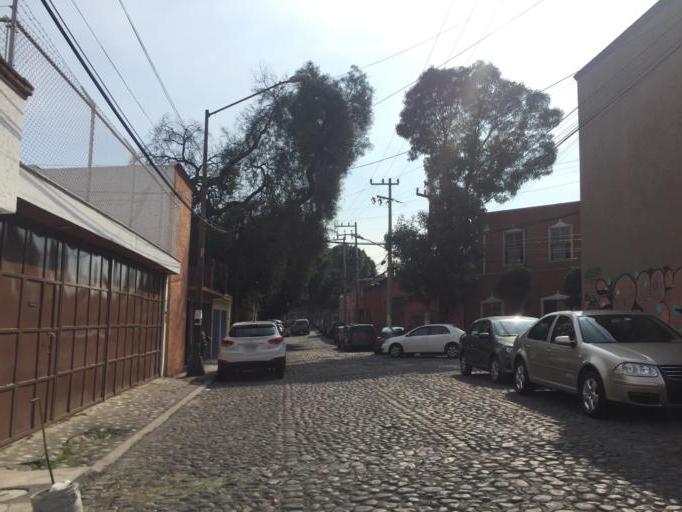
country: MX
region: Mexico City
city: Coyoacan
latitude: 19.3454
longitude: -99.1565
